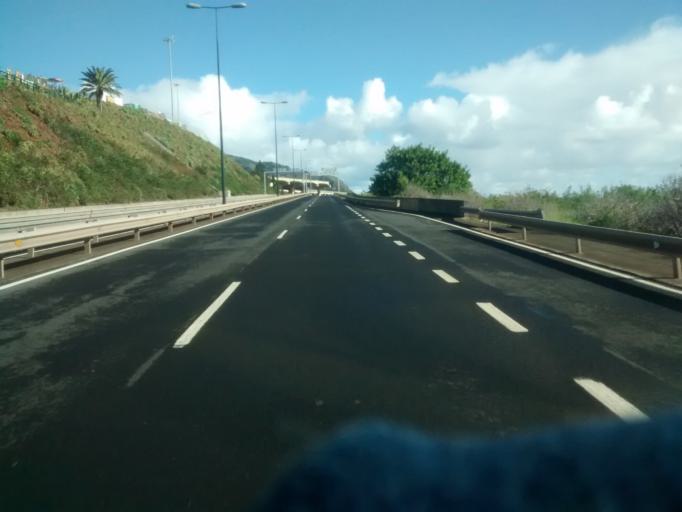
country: PT
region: Madeira
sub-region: Machico
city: Machico
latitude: 32.6940
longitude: -16.7734
